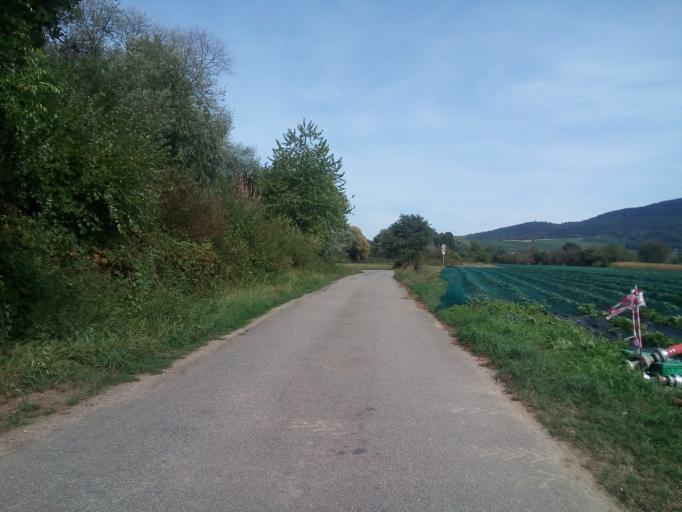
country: DE
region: Baden-Wuerttemberg
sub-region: Karlsruhe Region
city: Sinzheim
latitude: 48.7530
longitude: 8.1479
